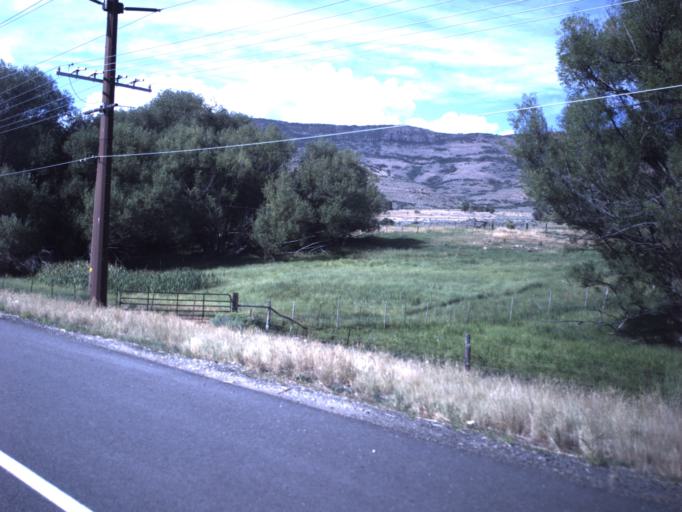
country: US
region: Utah
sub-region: Wasatch County
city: Heber
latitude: 40.5343
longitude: -111.4096
